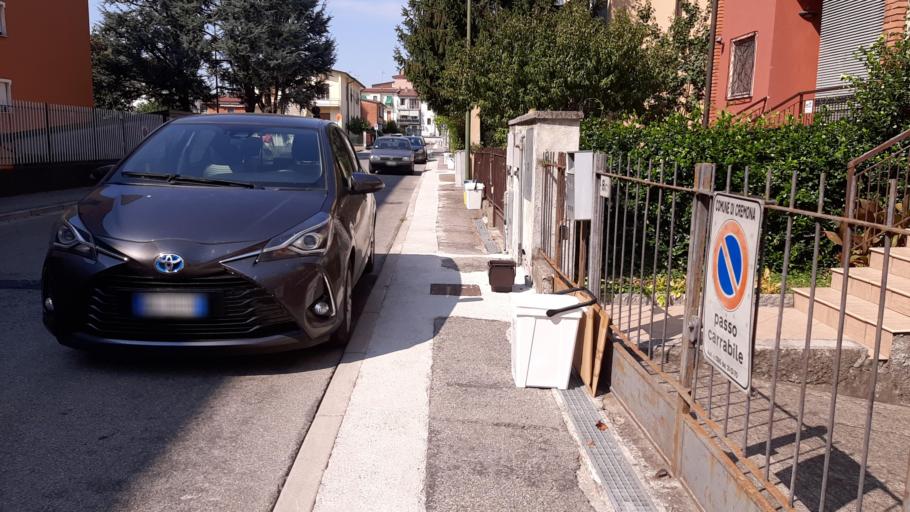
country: IT
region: Lombardy
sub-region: Provincia di Cremona
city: Cremona
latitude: 45.1364
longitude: 10.0397
